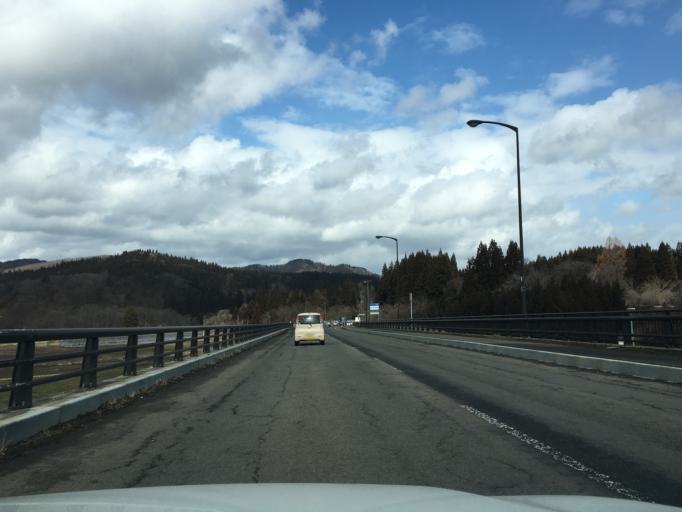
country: JP
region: Akita
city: Takanosu
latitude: 40.0250
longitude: 140.2741
